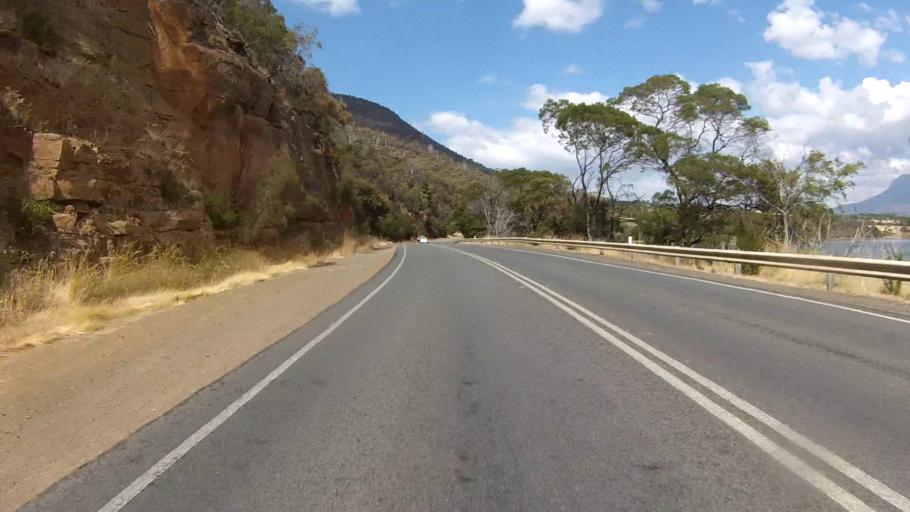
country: AU
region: Tasmania
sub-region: Brighton
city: Old Beach
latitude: -42.7879
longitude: 147.2917
